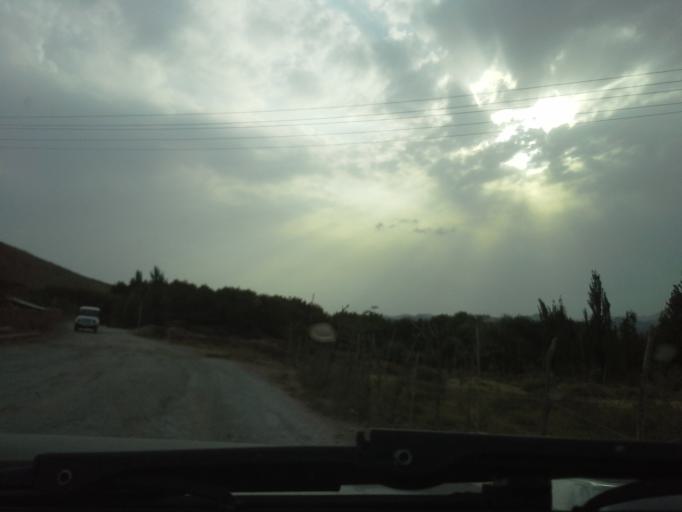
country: UZ
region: Qashqadaryo
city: Qorashina
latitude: 37.9256
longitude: 66.4927
